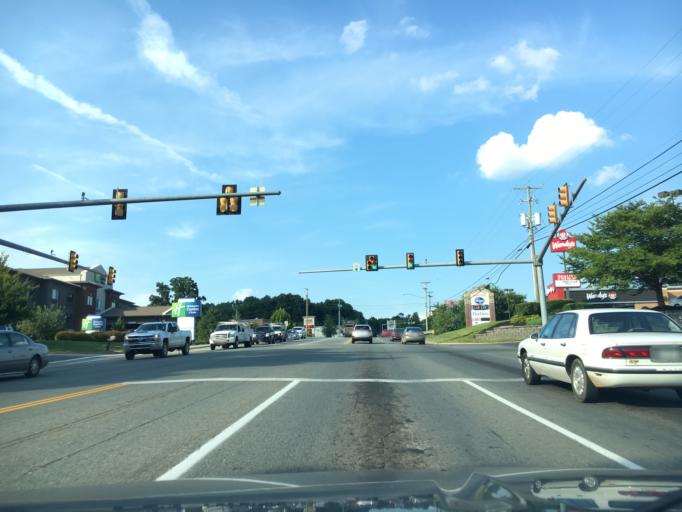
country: US
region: Virginia
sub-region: Franklin County
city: Rocky Mount
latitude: 37.0133
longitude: -79.8679
